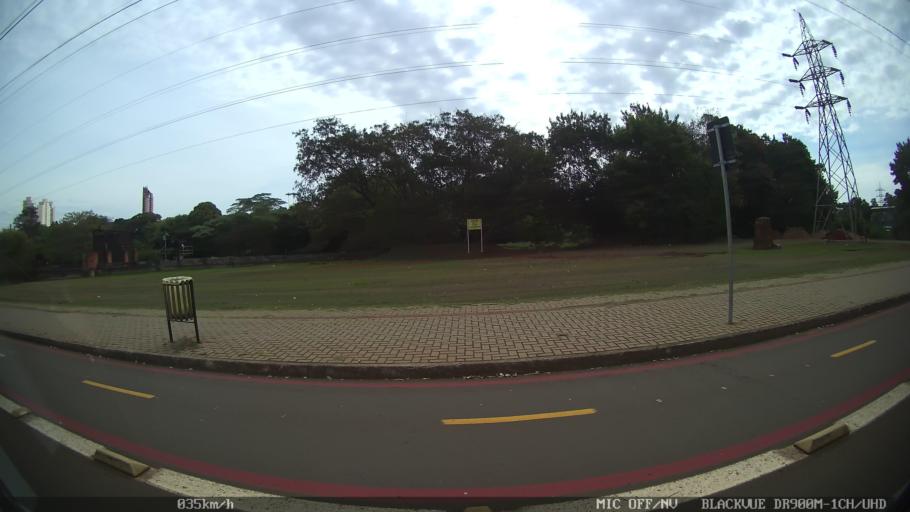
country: BR
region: Sao Paulo
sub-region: Piracicaba
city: Piracicaba
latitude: -22.7165
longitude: -47.6508
